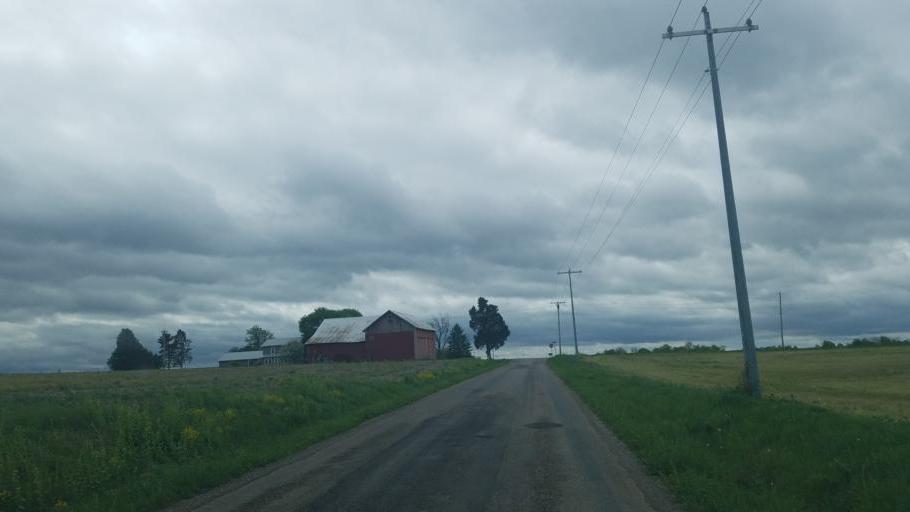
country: US
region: Ohio
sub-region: Sandusky County
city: Bellville
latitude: 40.5407
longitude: -82.4496
